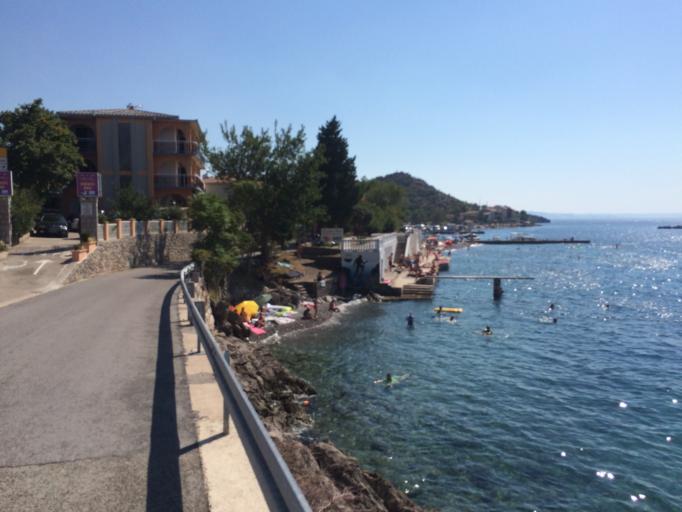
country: HR
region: Licko-Senjska
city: Senj
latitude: 44.9317
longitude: 14.9211
